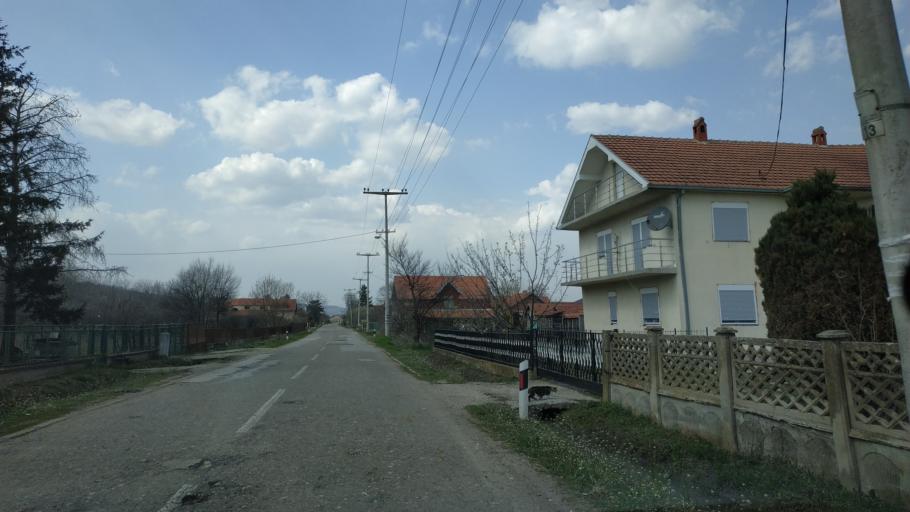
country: RS
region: Central Serbia
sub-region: Nisavski Okrug
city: Aleksinac
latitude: 43.5574
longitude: 21.6086
